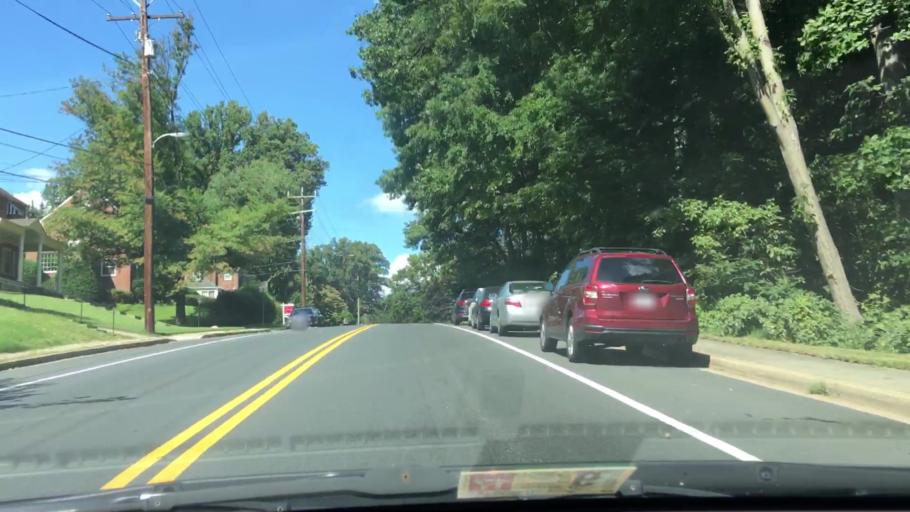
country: US
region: Maryland
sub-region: Montgomery County
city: South Kensington
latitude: 39.0135
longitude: -77.0902
